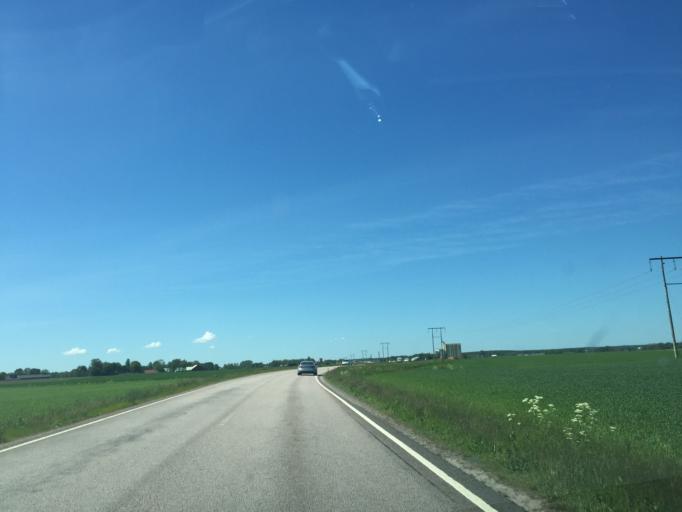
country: SE
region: OEstergoetland
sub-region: Mjolby Kommun
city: Mjolby
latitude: 58.3879
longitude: 15.1287
